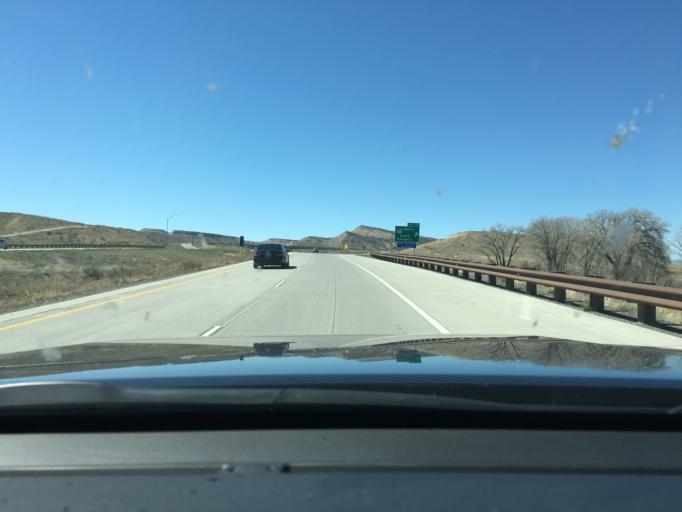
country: US
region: Colorado
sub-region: Mesa County
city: Loma
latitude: 39.1779
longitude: -108.8067
